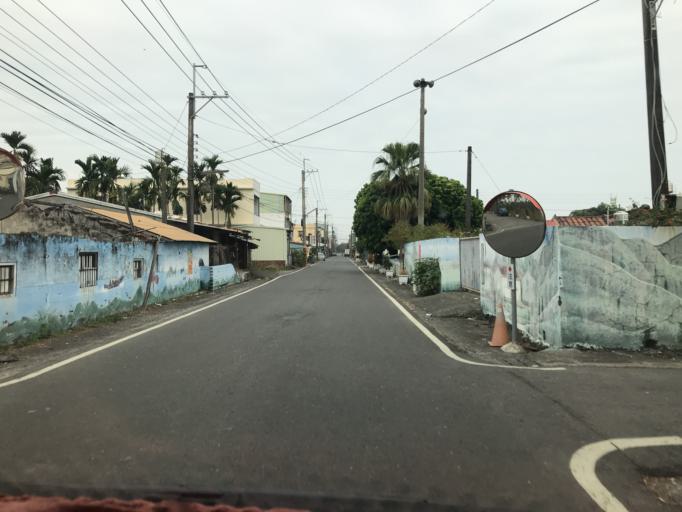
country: TW
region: Taiwan
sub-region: Pingtung
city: Pingtung
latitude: 22.5047
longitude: 120.5877
